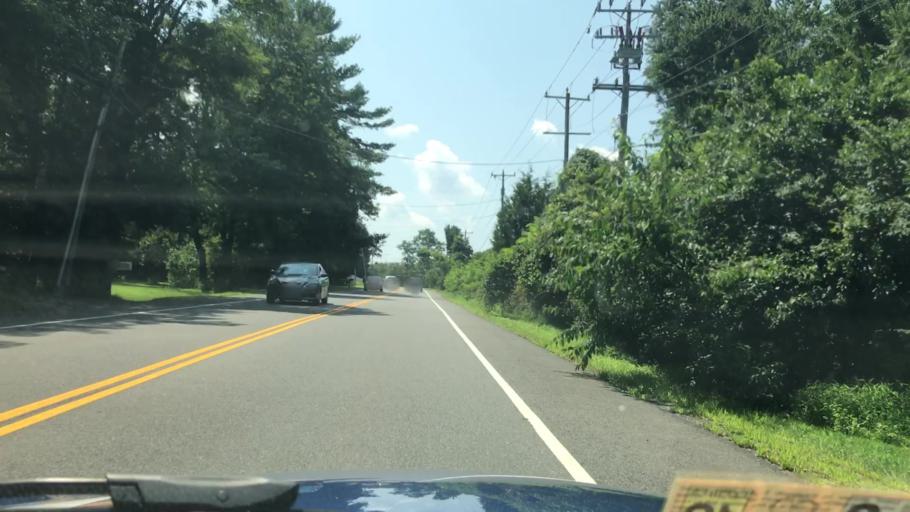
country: US
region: Virginia
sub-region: Fairfax County
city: Wolf Trap
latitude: 38.9167
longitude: -77.3038
